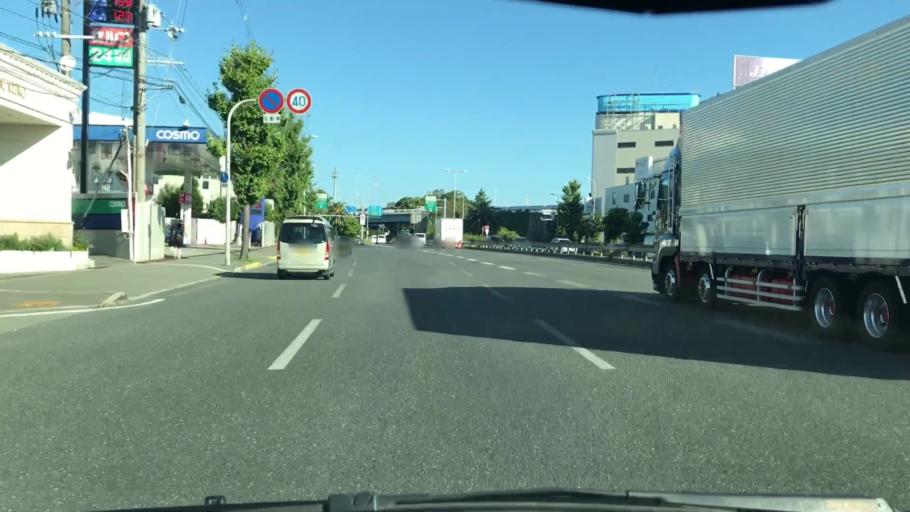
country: JP
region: Osaka
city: Ikeda
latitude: 34.7972
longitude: 135.4416
